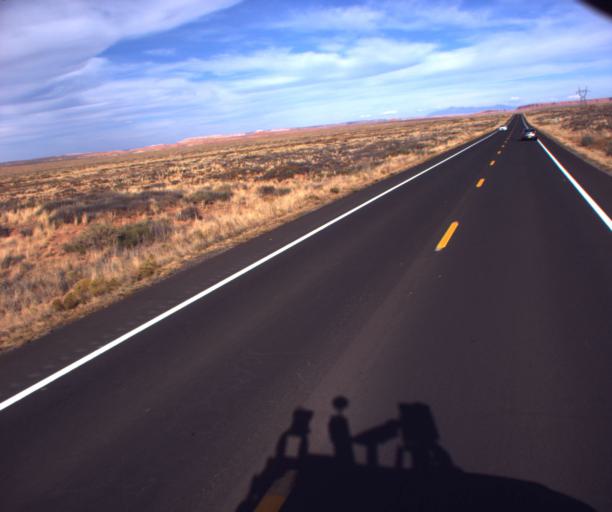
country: US
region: Arizona
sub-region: Apache County
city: Lukachukai
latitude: 36.9584
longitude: -109.4958
